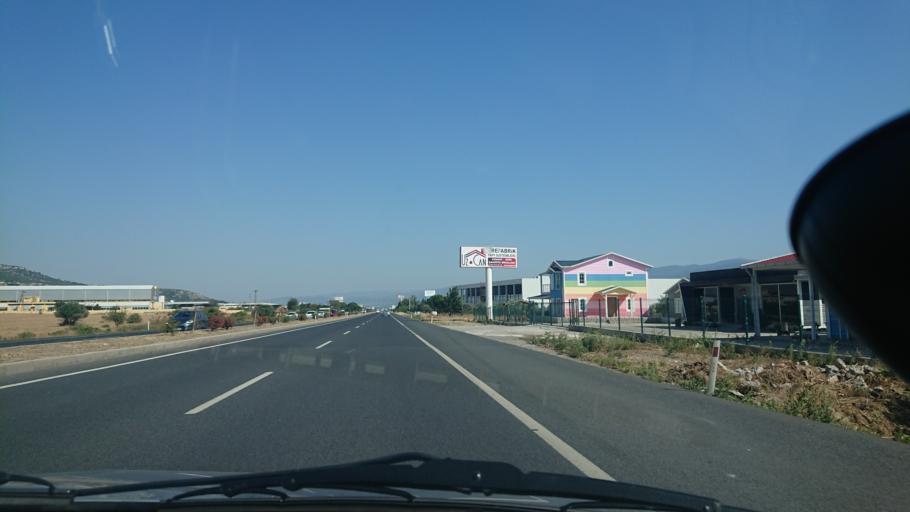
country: TR
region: Izmir
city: Kemalpasa
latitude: 38.4527
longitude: 27.4673
